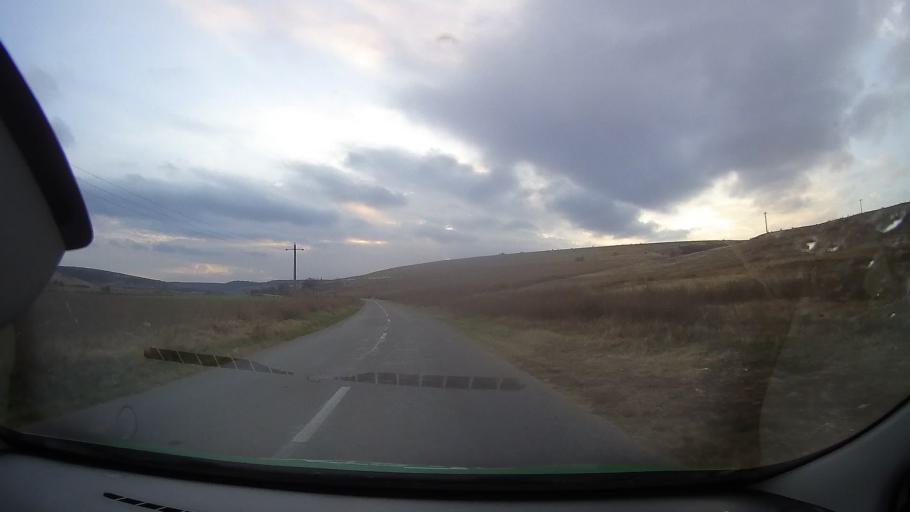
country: RO
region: Constanta
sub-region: Comuna Dobromir
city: Dobromir
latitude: 44.0299
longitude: 27.7975
